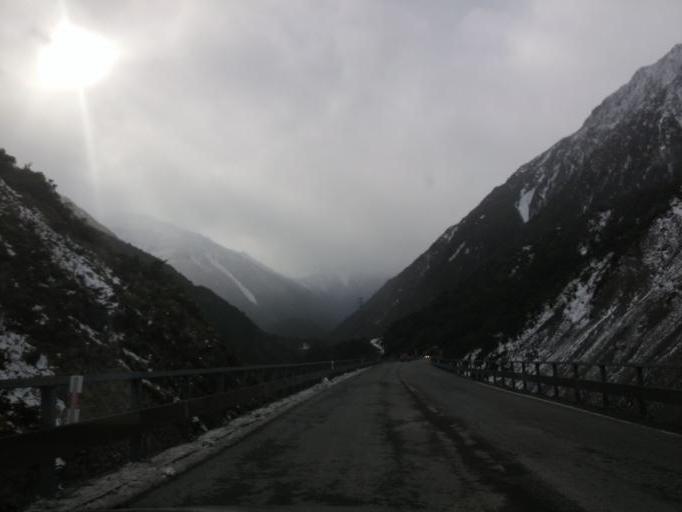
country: NZ
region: West Coast
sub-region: Grey District
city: Greymouth
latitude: -42.8876
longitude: 171.5552
